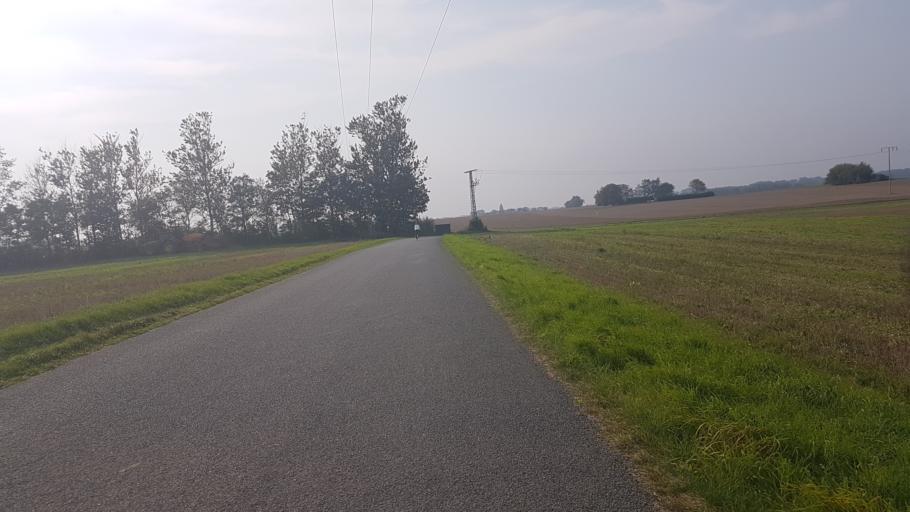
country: DE
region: Mecklenburg-Vorpommern
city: Garz
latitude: 54.2949
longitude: 13.3661
